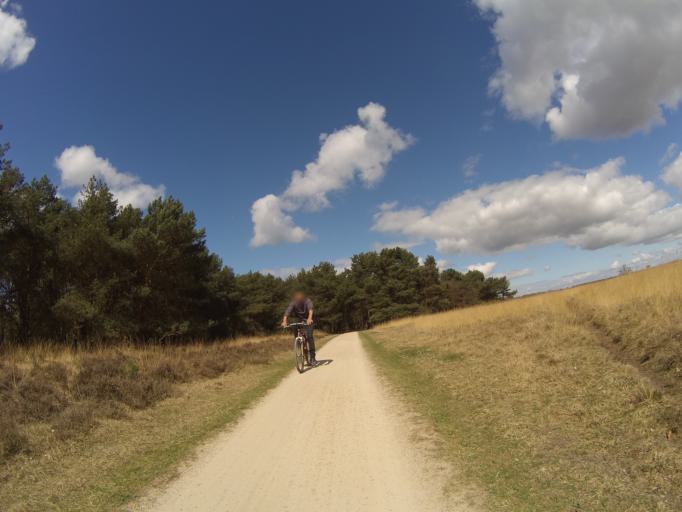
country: NL
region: North Holland
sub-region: Gemeente Bussum
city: Bussum
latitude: 52.2551
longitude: 5.1752
